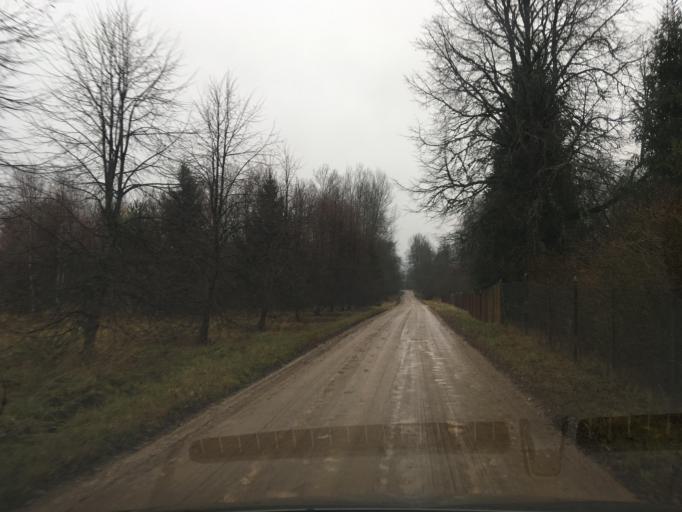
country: EE
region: Tartu
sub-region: Alatskivi vald
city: Kallaste
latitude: 58.3818
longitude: 27.0336
